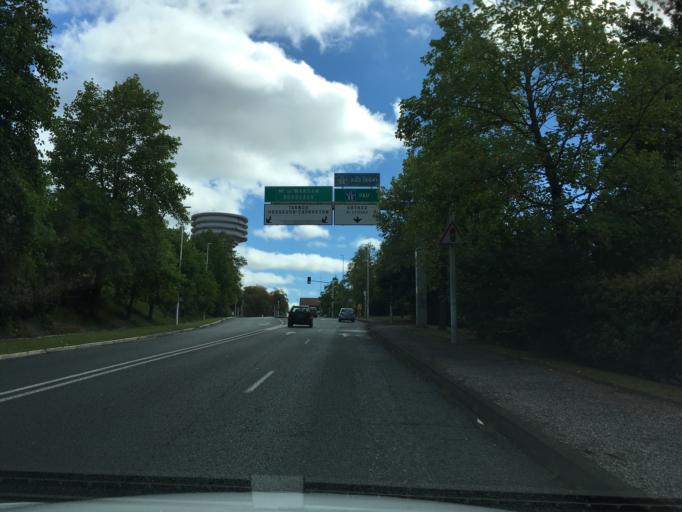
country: FR
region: Aquitaine
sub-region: Departement des Pyrenees-Atlantiques
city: Bayonne
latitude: 43.5037
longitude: -1.4708
